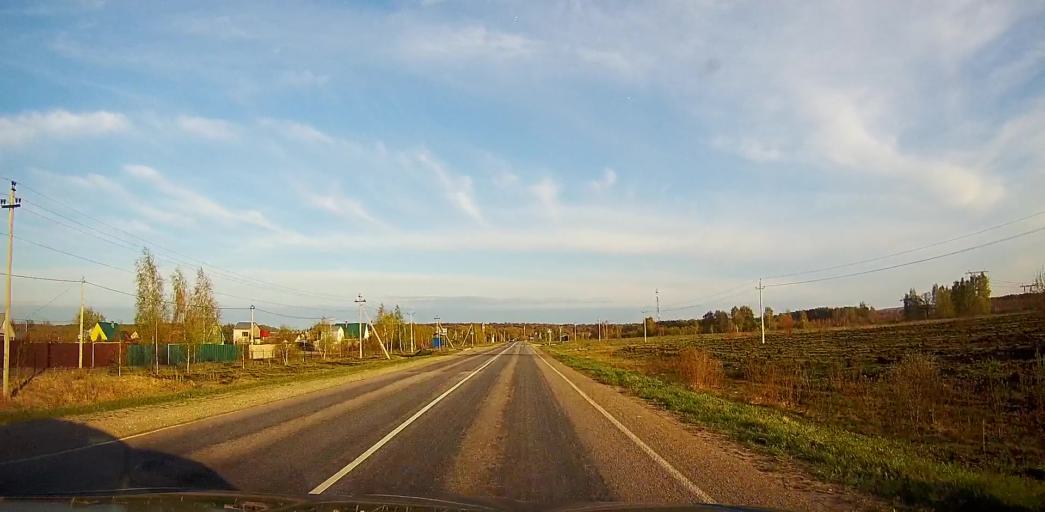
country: RU
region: Moskovskaya
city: Meshcherino
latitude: 55.2618
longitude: 38.2642
